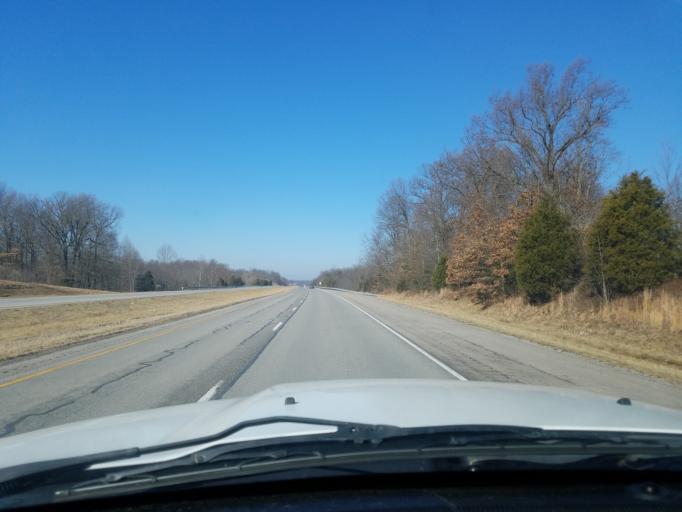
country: US
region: Kentucky
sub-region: Hardin County
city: Elizabethtown
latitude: 37.6306
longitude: -85.8228
